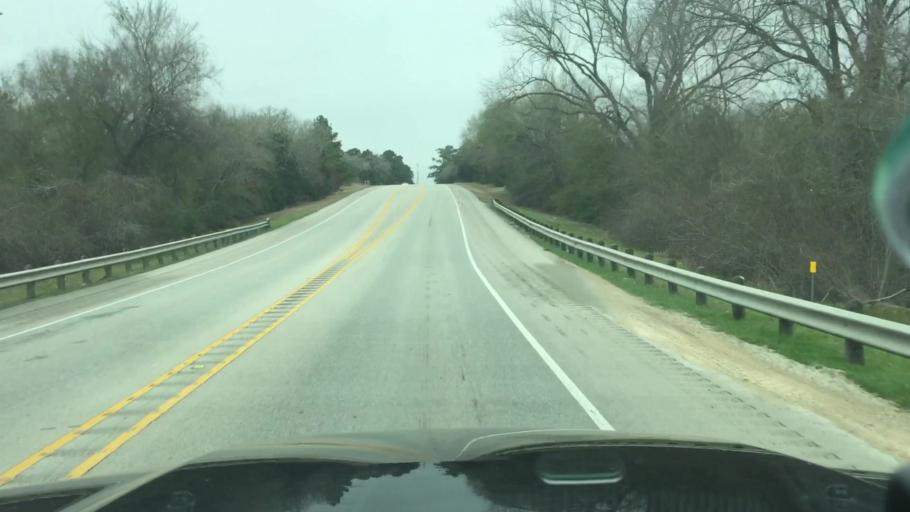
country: US
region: Texas
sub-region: Fayette County
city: La Grange
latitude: 30.0045
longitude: -96.8933
